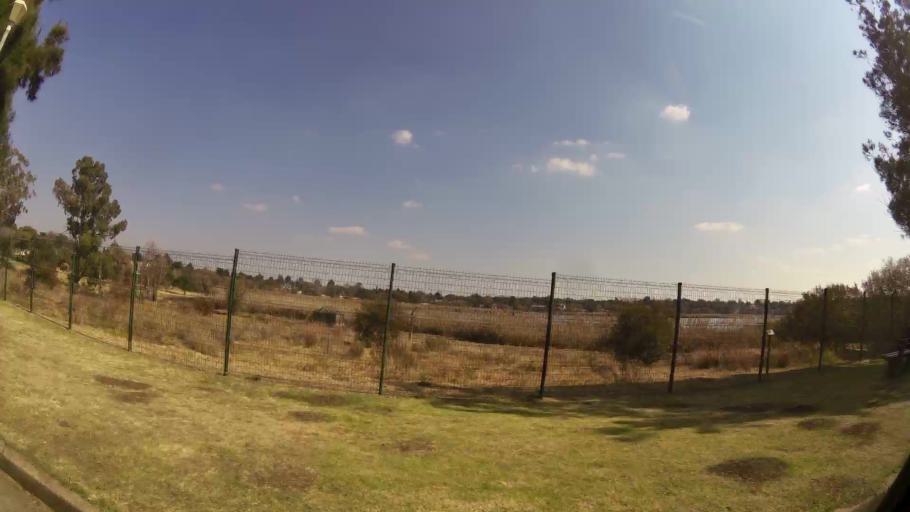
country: ZA
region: Gauteng
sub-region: Ekurhuleni Metropolitan Municipality
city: Benoni
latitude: -26.1933
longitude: 28.2977
